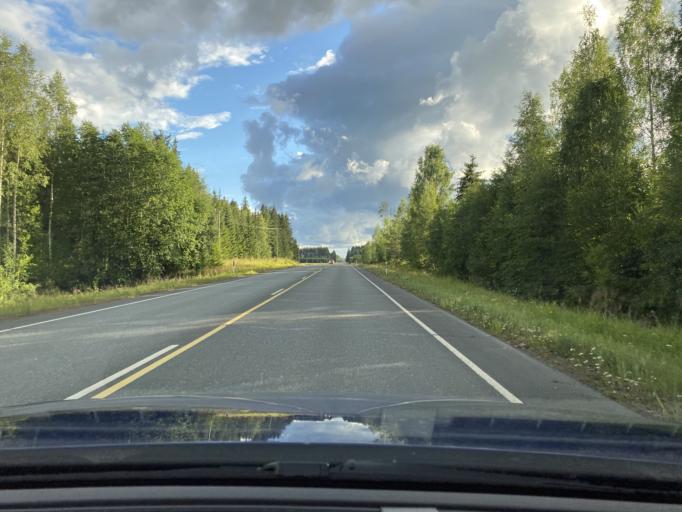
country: FI
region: Haeme
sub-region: Haemeenlinna
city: Renko
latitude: 60.8884
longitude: 24.2550
